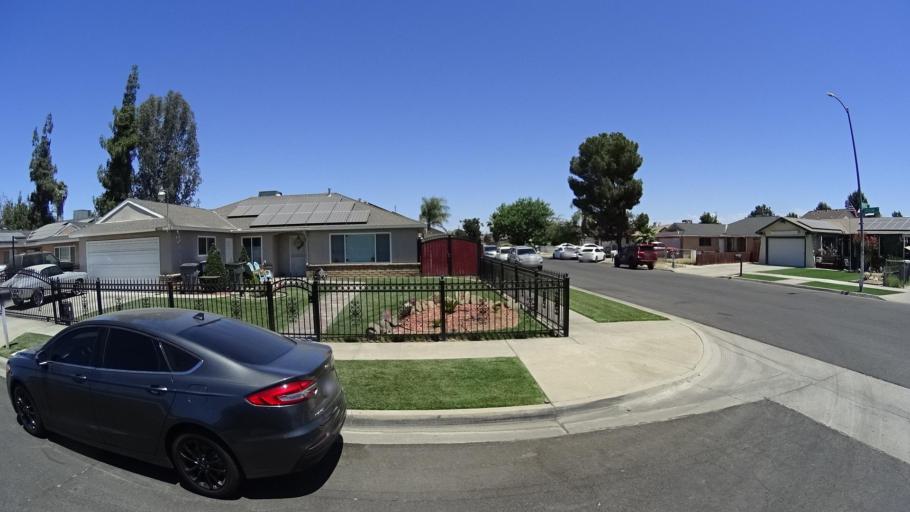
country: US
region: California
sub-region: Fresno County
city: Fresno
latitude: 36.7097
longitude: -119.7485
